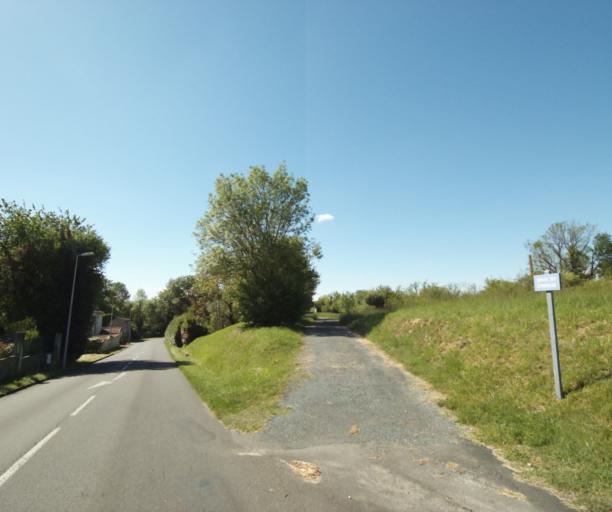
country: FR
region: Poitou-Charentes
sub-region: Departement de la Charente-Maritime
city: Bussac-sur-Charente
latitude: 45.8166
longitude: -0.6363
